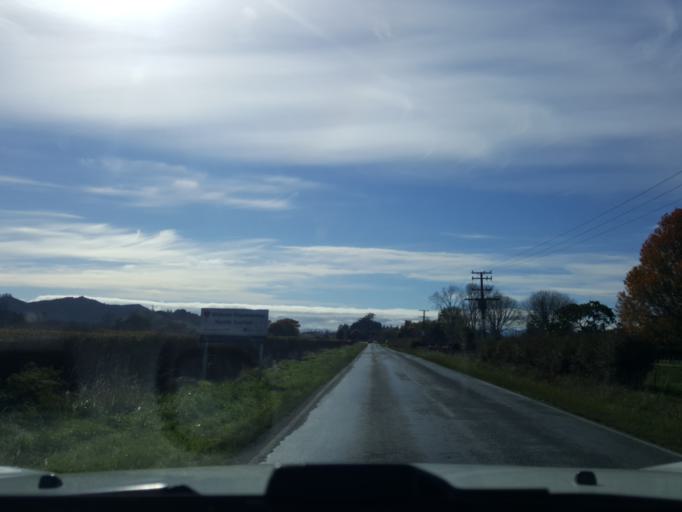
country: NZ
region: Waikato
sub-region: Waikato District
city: Ngaruawahia
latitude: -37.6049
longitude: 175.1989
